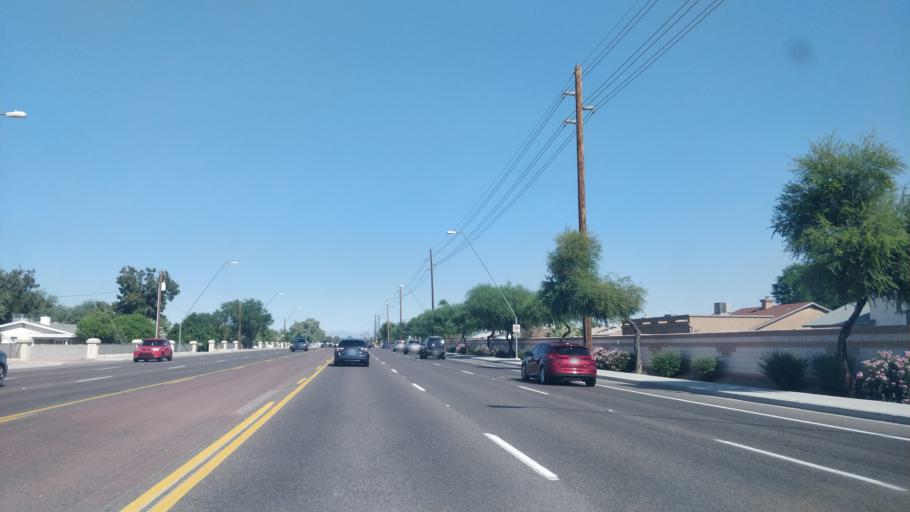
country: US
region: Arizona
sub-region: Maricopa County
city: Chandler
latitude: 33.3002
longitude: -111.8070
